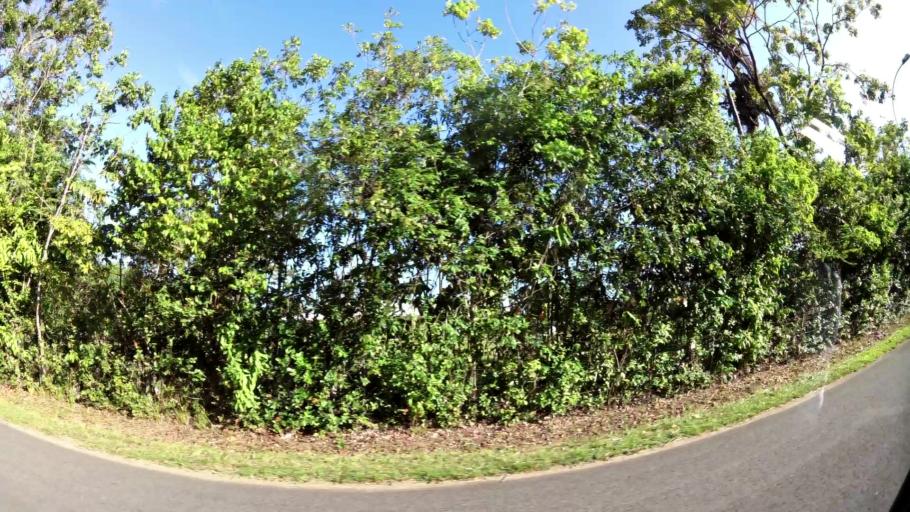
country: GF
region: Guyane
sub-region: Guyane
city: Remire-Montjoly
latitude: 4.9023
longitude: -52.2824
